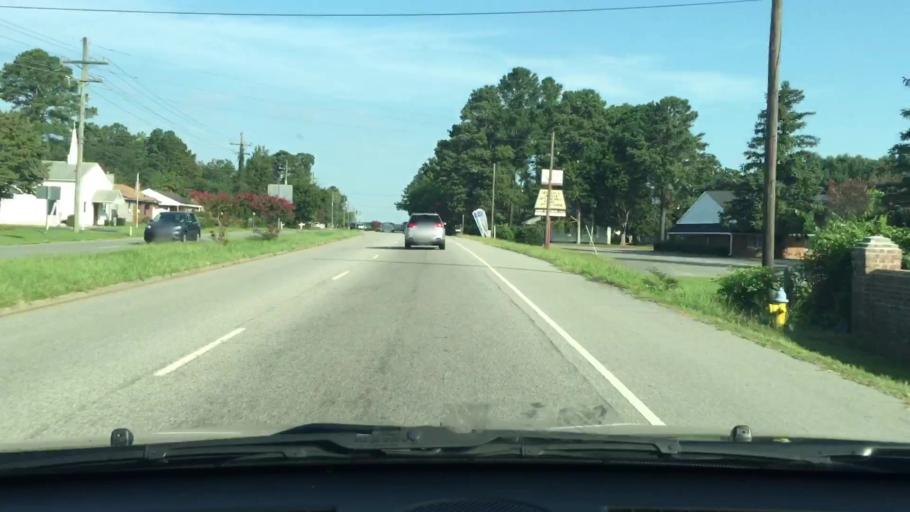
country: US
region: Virginia
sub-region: Isle of Wight County
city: Carrollton
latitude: 36.9417
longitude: -76.5891
